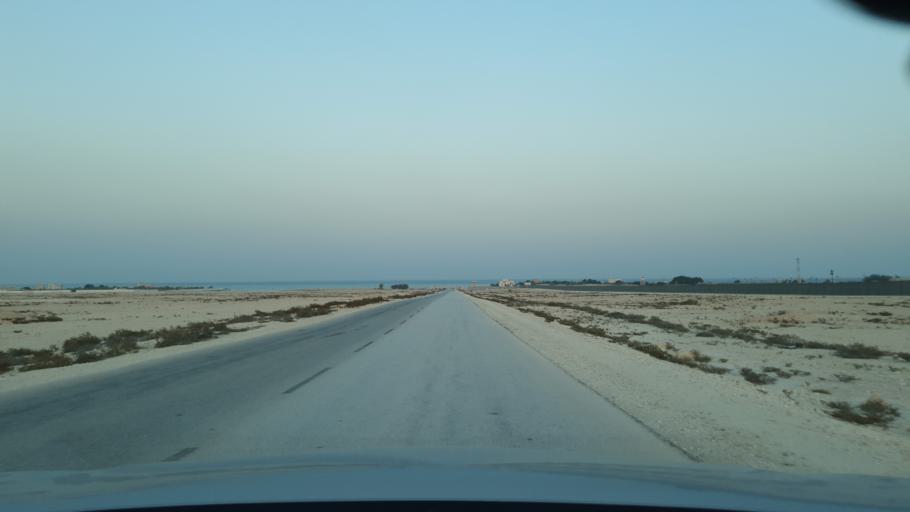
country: BH
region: Central Governorate
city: Dar Kulayb
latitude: 25.9558
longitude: 50.6021
